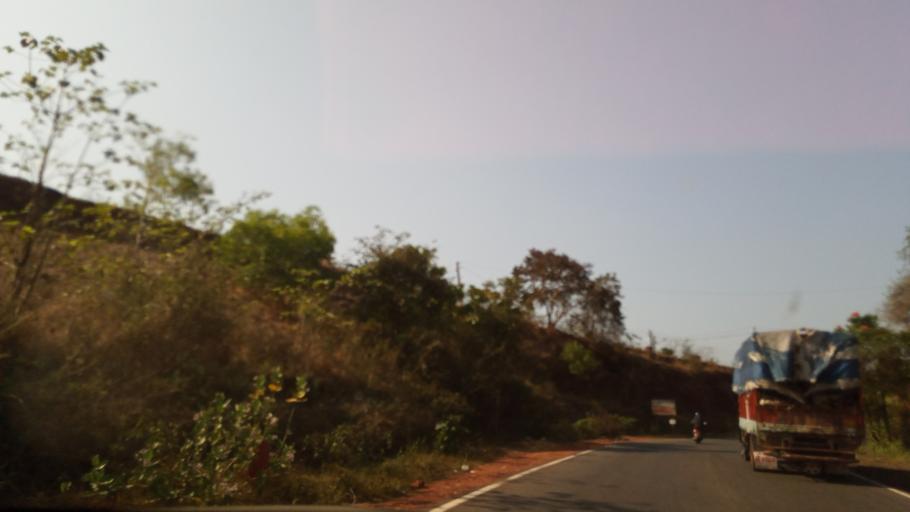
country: IN
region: Goa
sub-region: North Goa
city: Bandora
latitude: 15.4546
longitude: 73.9640
